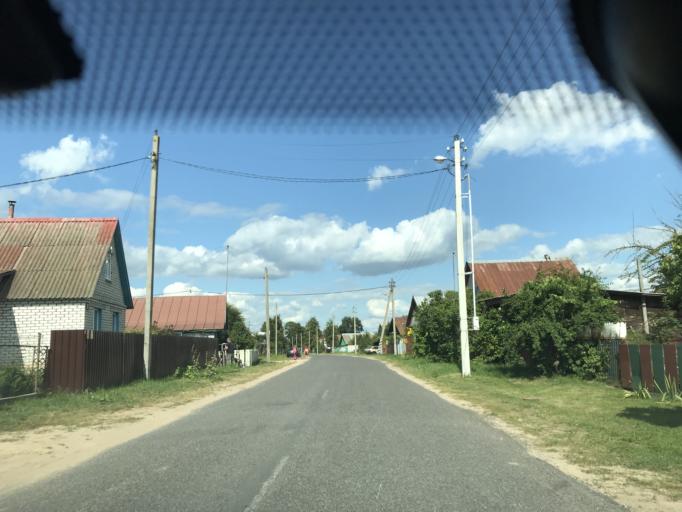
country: BY
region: Mogilev
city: Poselok Voskhod
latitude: 53.7839
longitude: 30.3513
